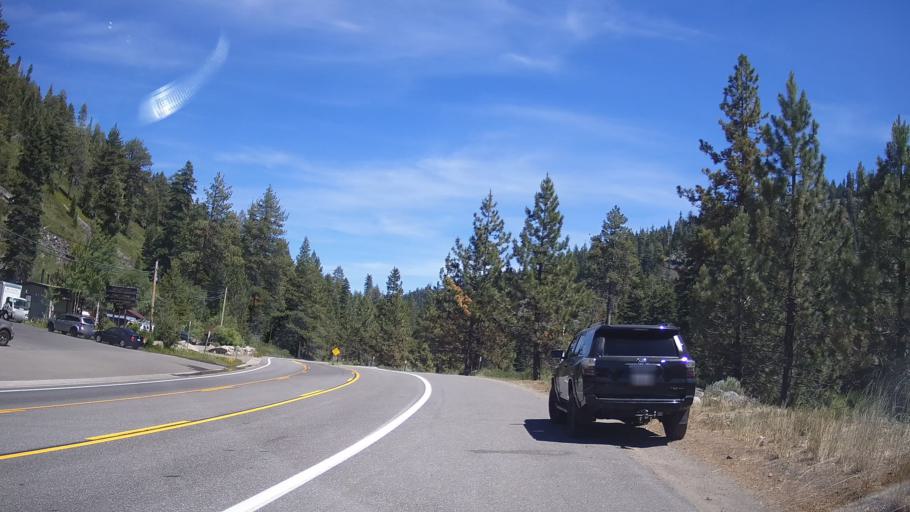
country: US
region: California
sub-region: Placer County
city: Sunnyside-Tahoe City
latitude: 39.1676
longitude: -120.1825
